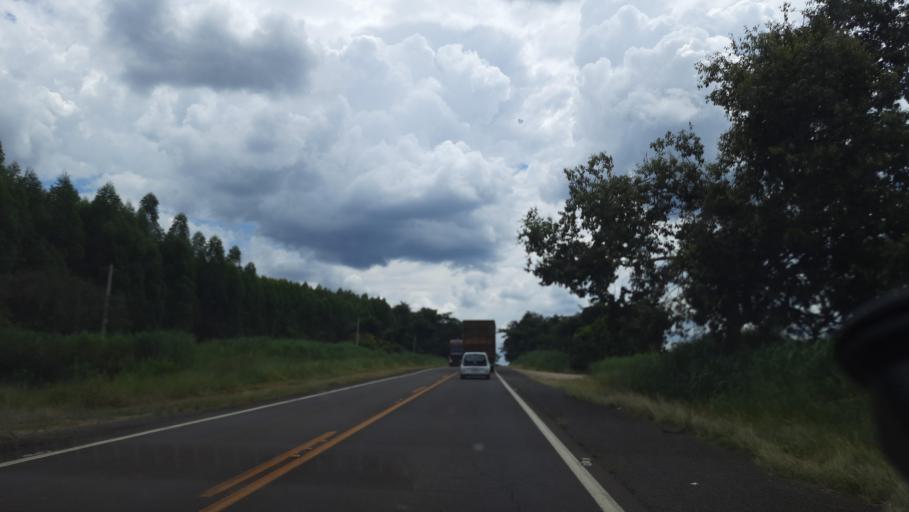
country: BR
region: Sao Paulo
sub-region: Mococa
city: Mococa
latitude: -21.4570
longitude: -47.1208
